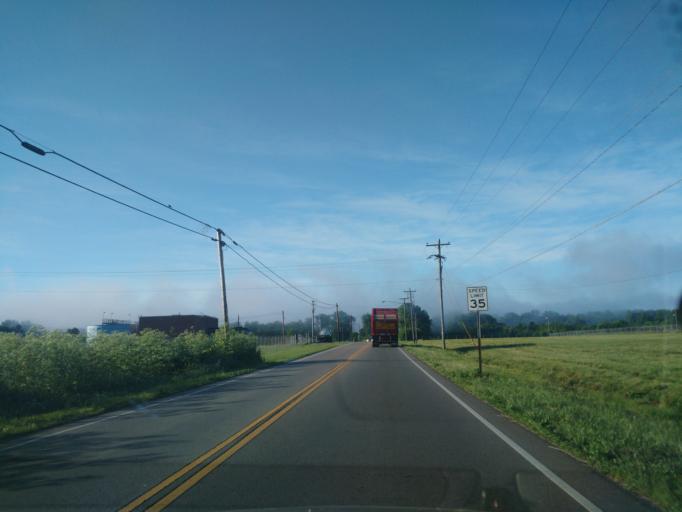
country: US
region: Ohio
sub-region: Pike County
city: Waverly
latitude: 39.1119
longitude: -82.9814
